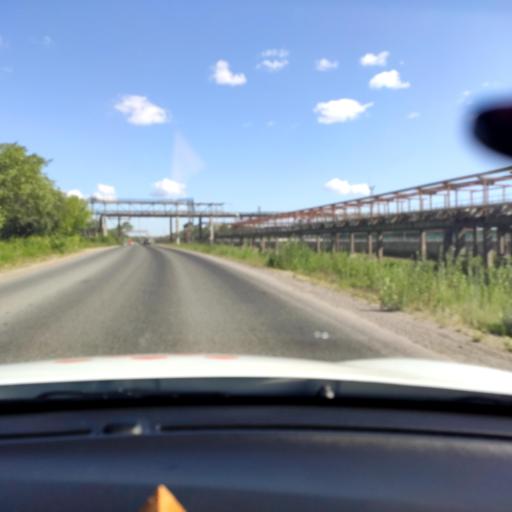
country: RU
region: Tatarstan
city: Staroye Arakchino
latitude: 55.8778
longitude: 48.9760
